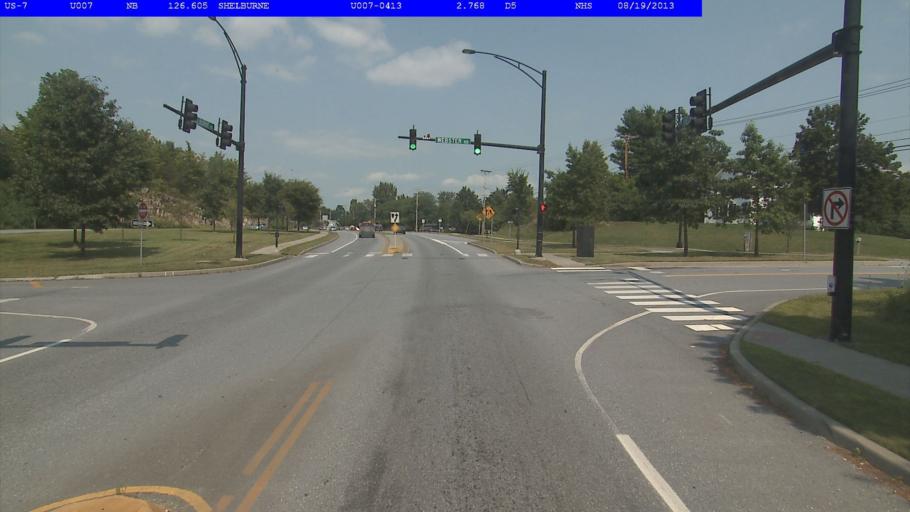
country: US
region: Vermont
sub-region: Chittenden County
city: Burlington
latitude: 44.3906
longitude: -73.2220
